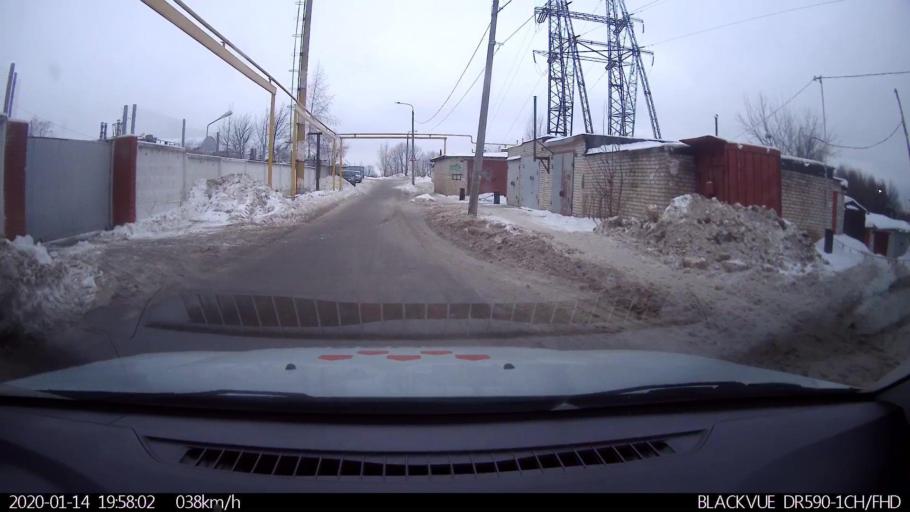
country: RU
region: Nizjnij Novgorod
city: Nizhniy Novgorod
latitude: 56.2359
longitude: 43.9403
